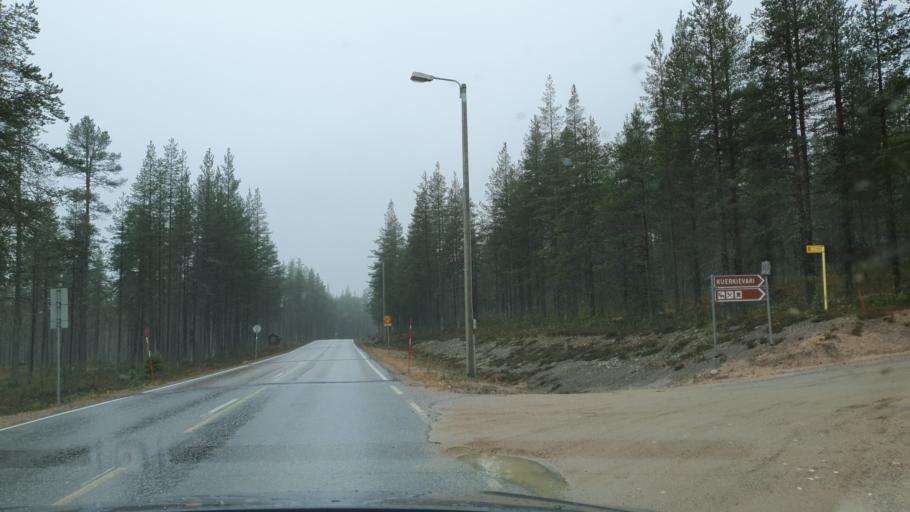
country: FI
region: Lapland
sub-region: Tunturi-Lappi
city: Kolari
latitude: 67.5974
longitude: 24.1193
